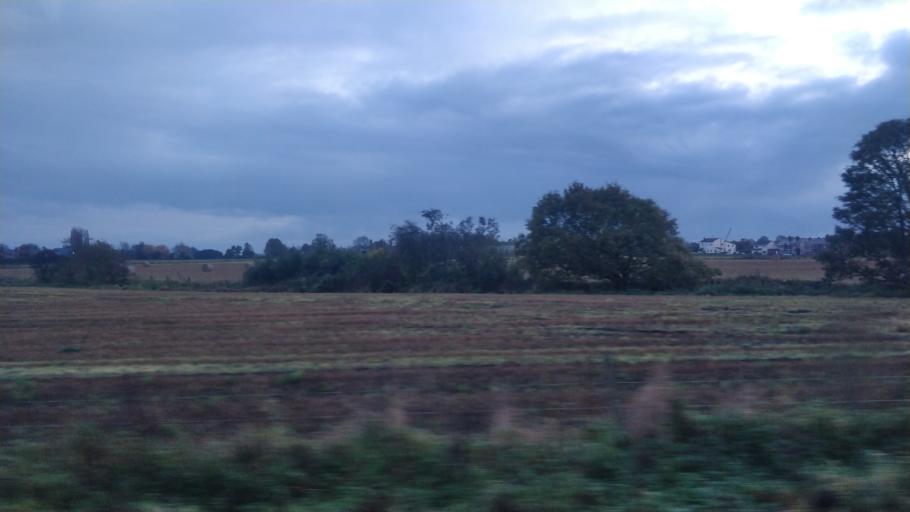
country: GB
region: England
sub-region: Lancashire
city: Ormskirk
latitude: 53.6098
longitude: -2.8604
